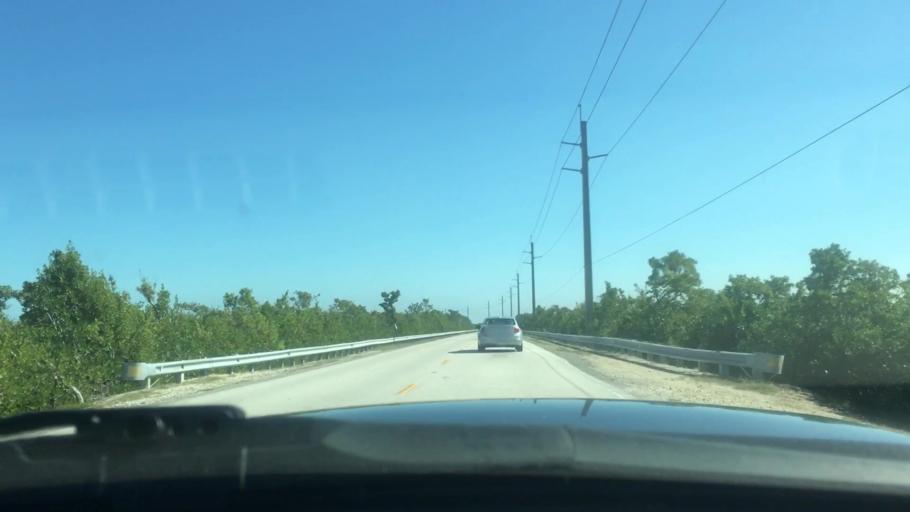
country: US
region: Florida
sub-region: Monroe County
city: North Key Largo
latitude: 25.2840
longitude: -80.3176
